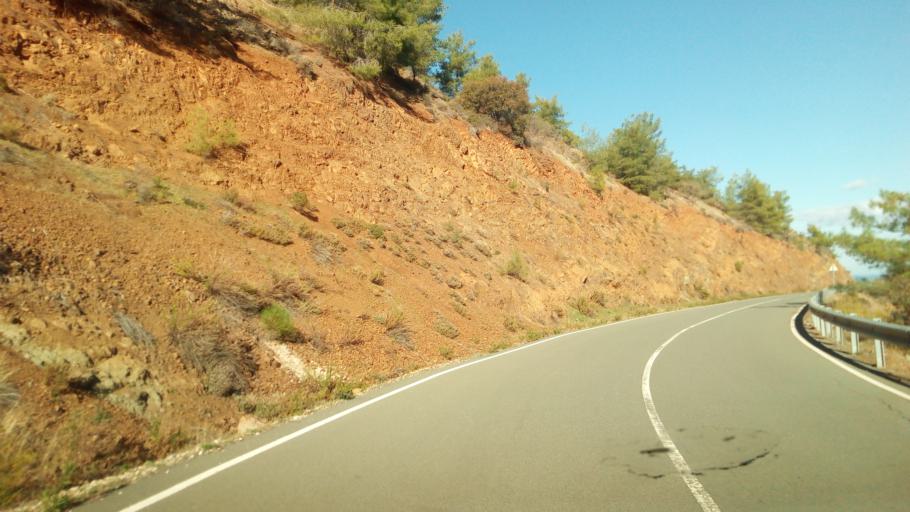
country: CY
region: Lefkosia
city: Lefka
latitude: 35.1024
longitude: 32.7572
